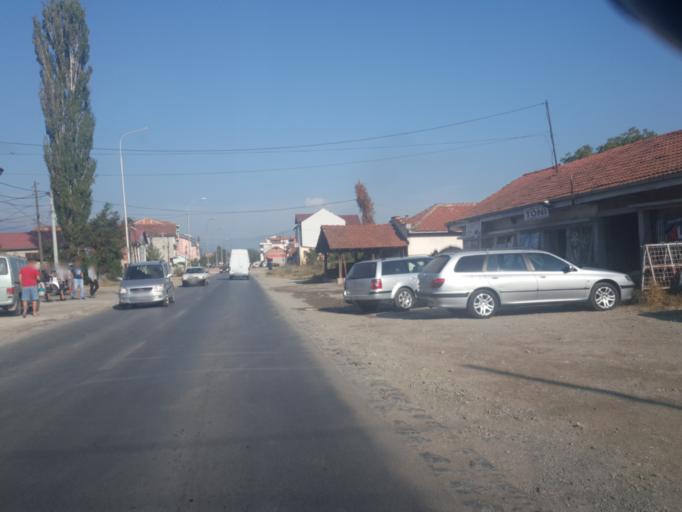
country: XK
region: Gjakova
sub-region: Komuna e Gjakoves
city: Gjakove
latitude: 42.4018
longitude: 20.4141
